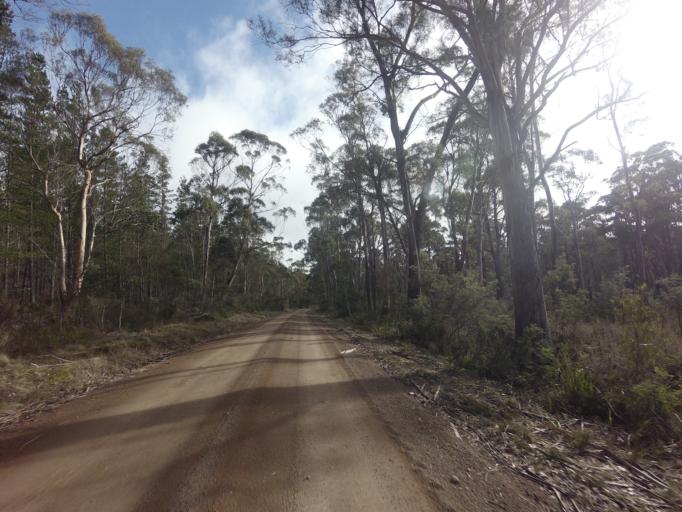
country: AU
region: Tasmania
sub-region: Derwent Valley
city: New Norfolk
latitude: -42.7625
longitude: 146.8954
